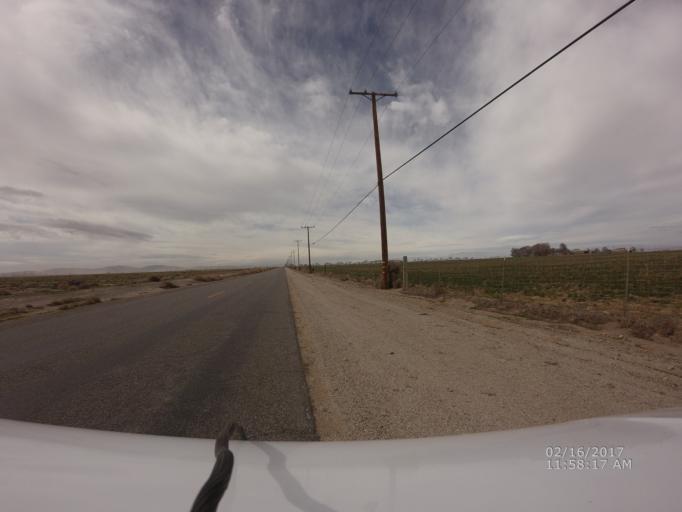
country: US
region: California
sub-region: Los Angeles County
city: Lake Los Angeles
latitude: 34.6900
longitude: -117.9220
